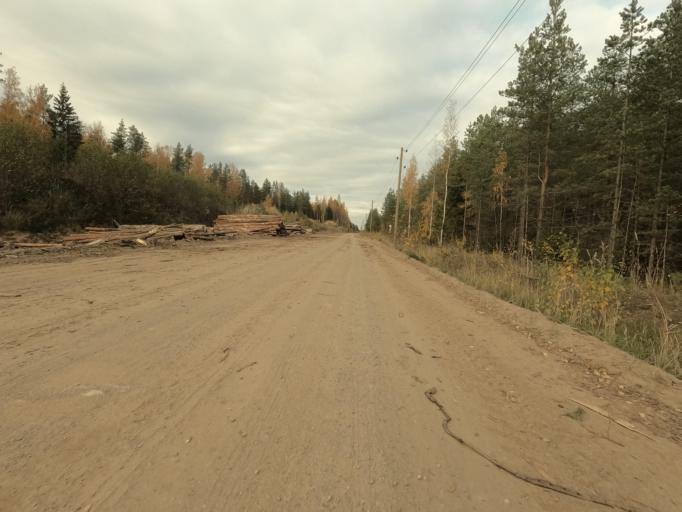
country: RU
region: Leningrad
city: Priladozhskiy
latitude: 59.6910
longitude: 31.3609
